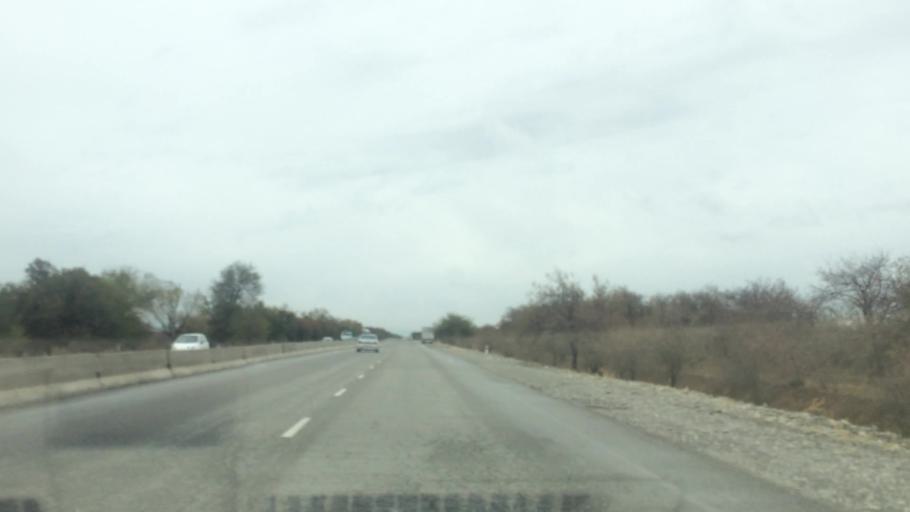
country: UZ
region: Samarqand
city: Bulung'ur
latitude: 39.8183
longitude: 67.3840
